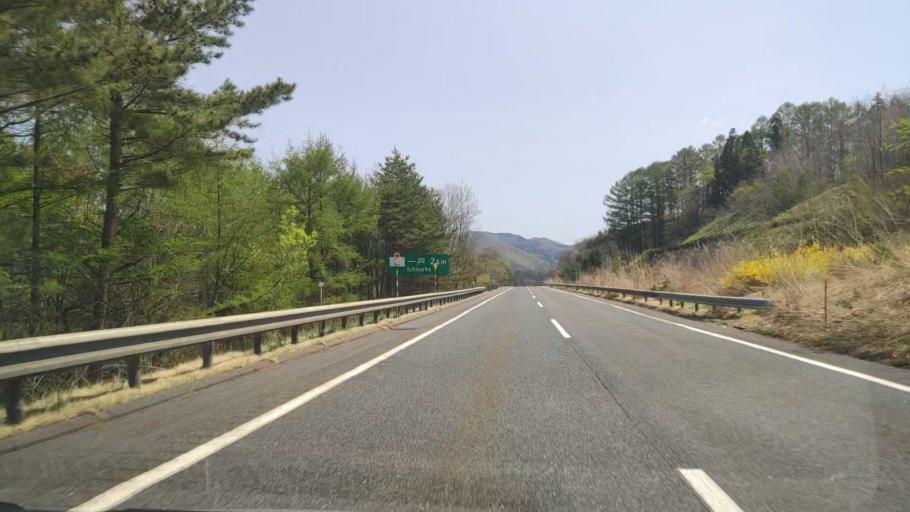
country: JP
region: Iwate
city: Ichinohe
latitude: 40.2269
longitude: 141.2713
